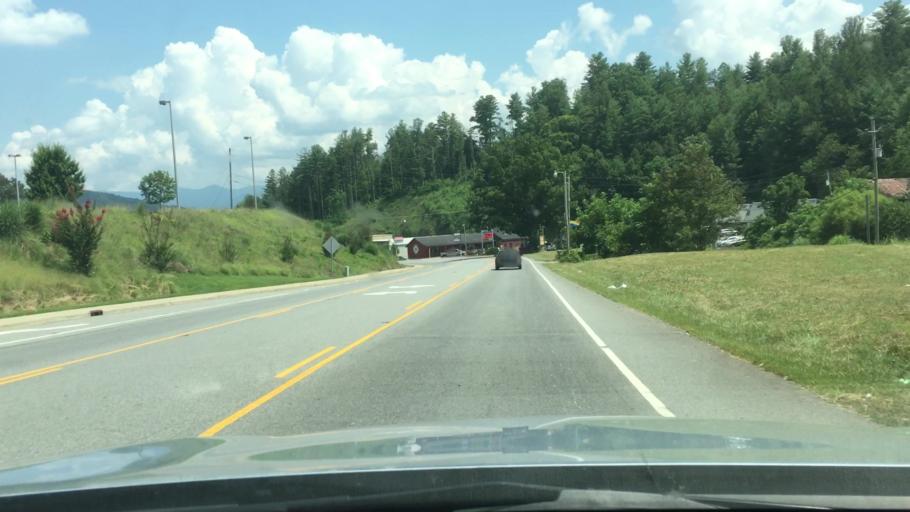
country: US
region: North Carolina
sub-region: Madison County
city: Mars Hill
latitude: 35.8243
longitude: -82.5453
